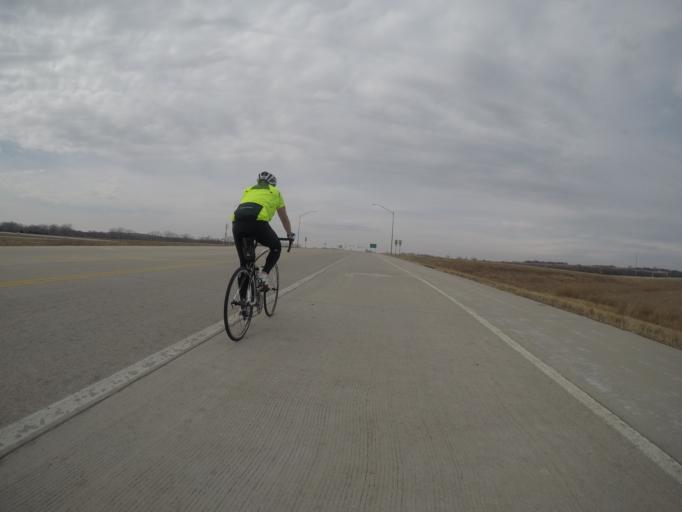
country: US
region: Kansas
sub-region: Riley County
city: Ogden
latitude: 39.1131
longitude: -96.6940
